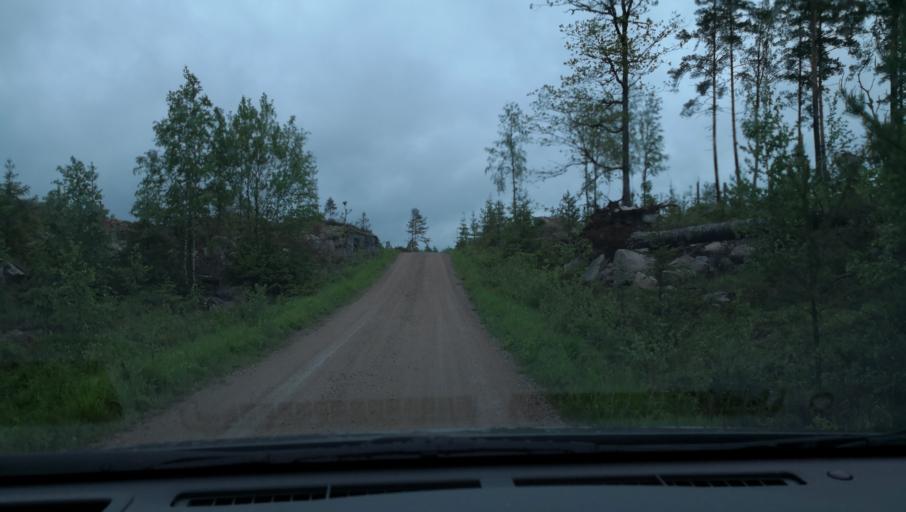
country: SE
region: Uppsala
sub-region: Enkopings Kommun
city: Orsundsbro
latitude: 59.9374
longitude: 17.3124
